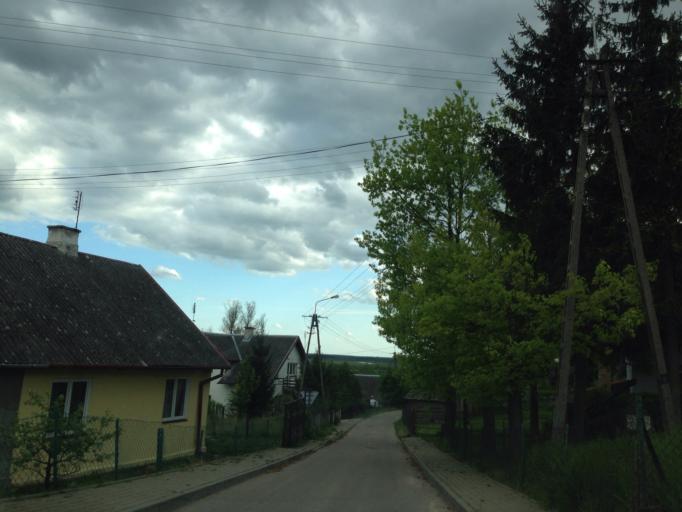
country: PL
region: Podlasie
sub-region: Powiat lomzynski
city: Wizna
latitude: 53.1909
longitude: 22.3852
